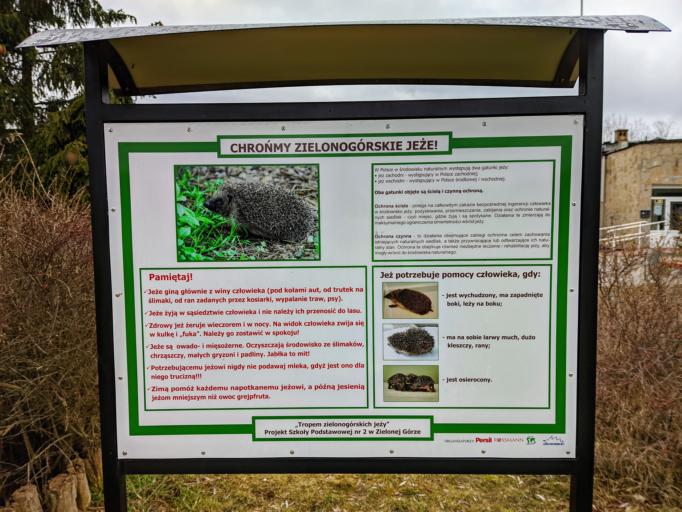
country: PL
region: Lubusz
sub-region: Zielona Gora
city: Zielona Gora
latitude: 51.9364
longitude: 15.4846
